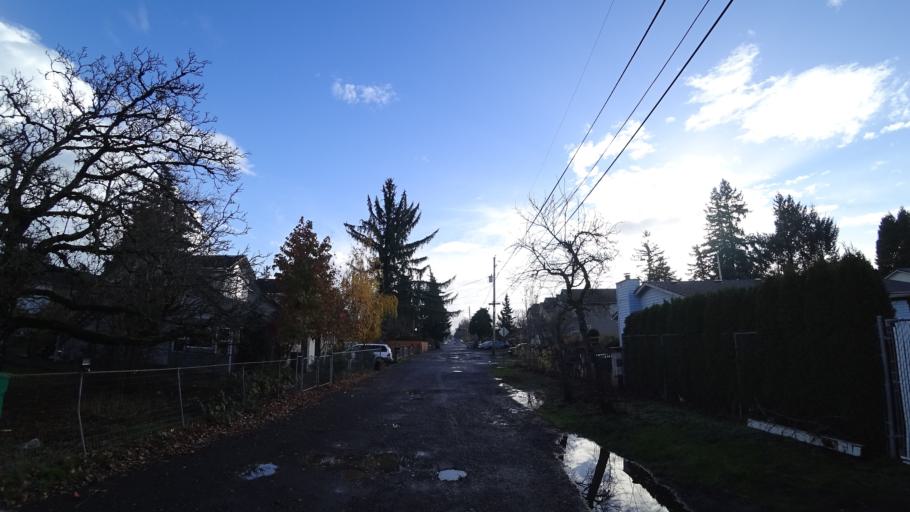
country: US
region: Oregon
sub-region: Multnomah County
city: Lents
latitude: 45.5237
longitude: -122.5429
